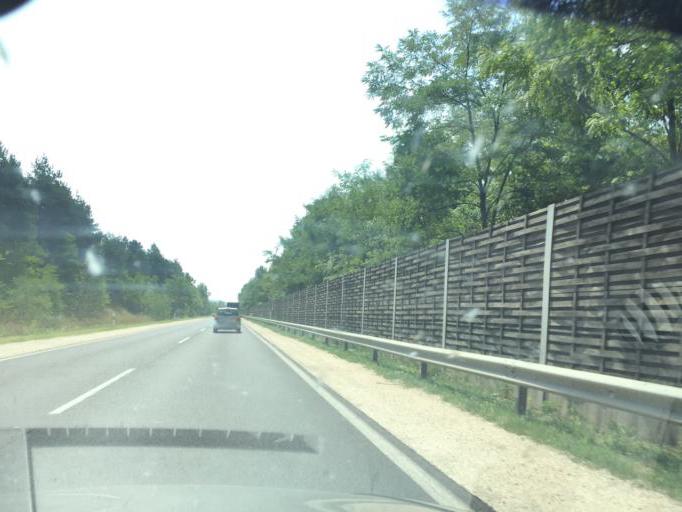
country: HU
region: Pest
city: Szod
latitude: 47.7066
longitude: 19.1652
